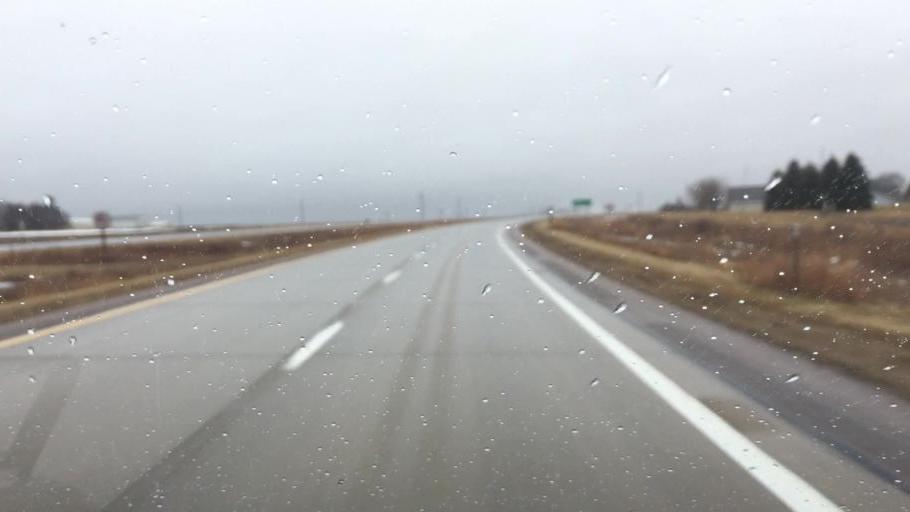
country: US
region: Iowa
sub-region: O'Brien County
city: Sheldon
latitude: 43.0725
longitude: -95.8972
